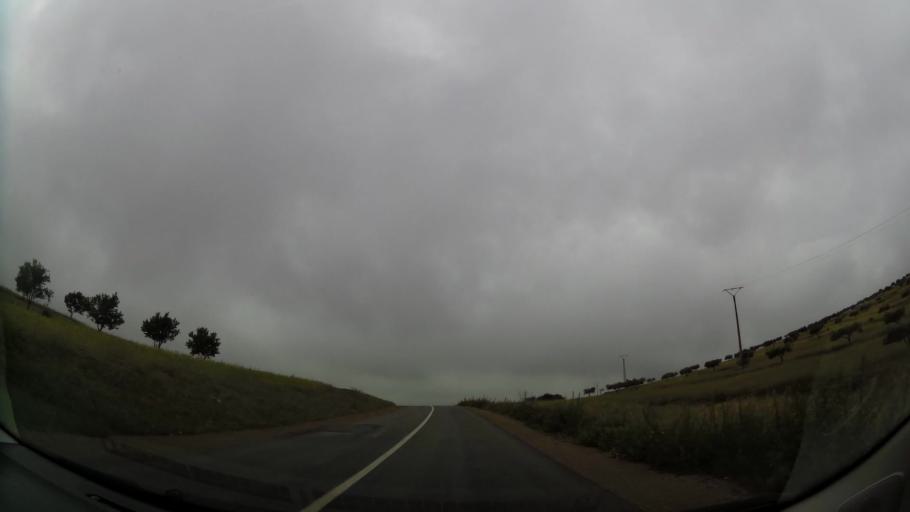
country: MA
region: Oriental
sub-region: Nador
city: Selouane
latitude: 35.1206
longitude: -3.0633
